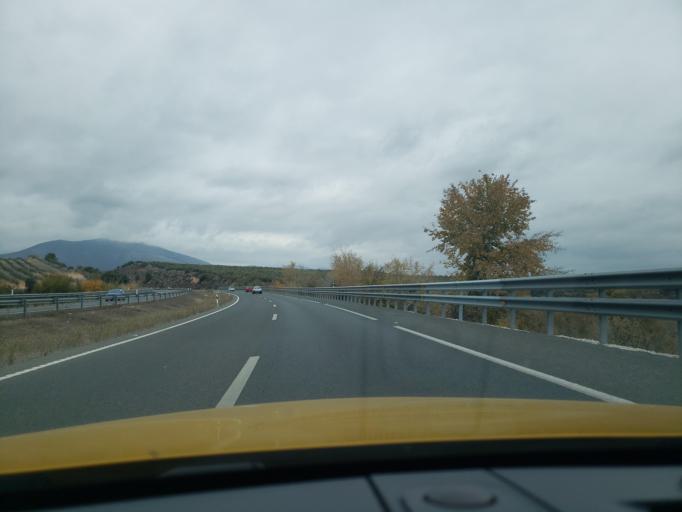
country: ES
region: Andalusia
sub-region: Provincia de Granada
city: Calicasas
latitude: 37.2929
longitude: -3.6565
